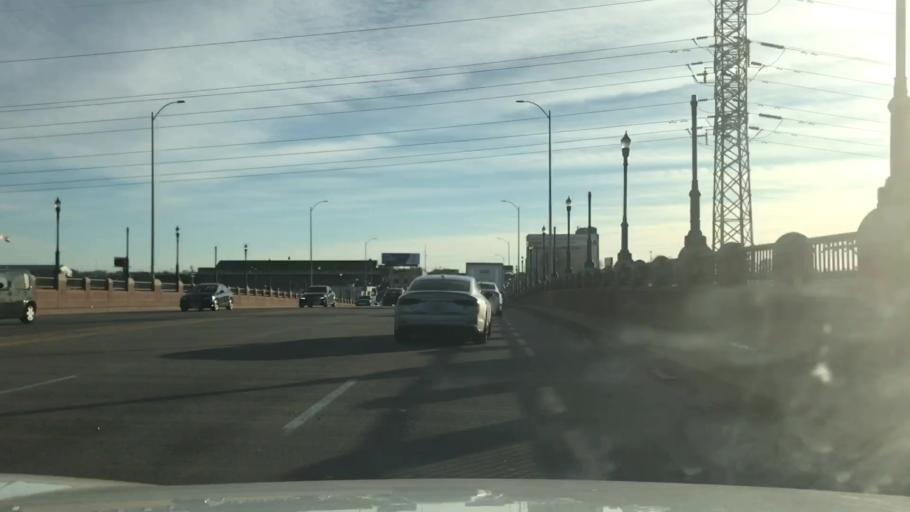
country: US
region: Missouri
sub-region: Saint Louis County
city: Richmond Heights
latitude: 38.6234
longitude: -90.2656
